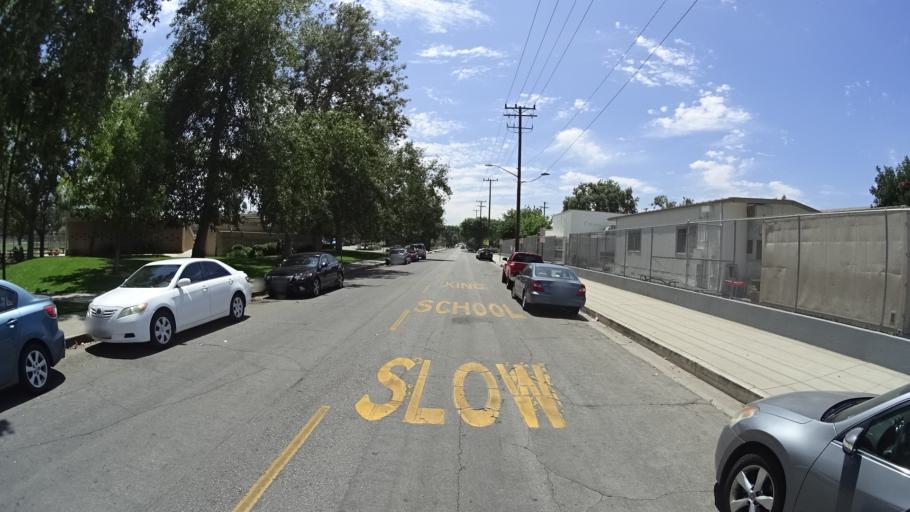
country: US
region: California
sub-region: Los Angeles County
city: Burbank
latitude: 34.1730
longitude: -118.3198
